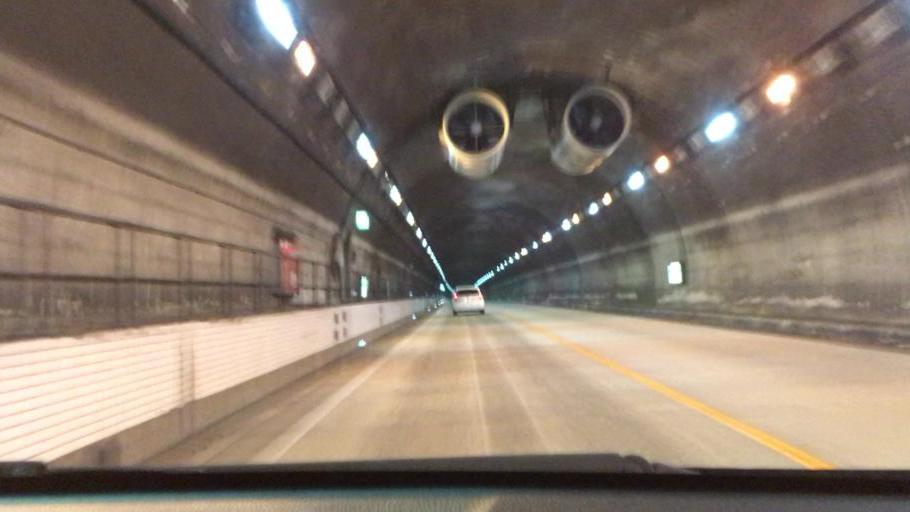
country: JP
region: Yamaguchi
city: Tokuyama
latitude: 34.0892
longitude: 131.7522
